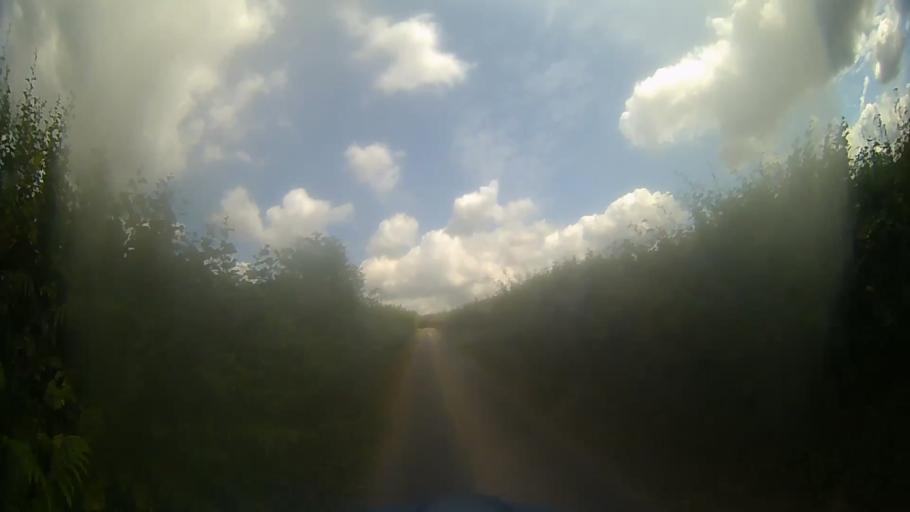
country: GB
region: England
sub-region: Hampshire
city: Andover
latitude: 51.2478
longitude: -1.4407
